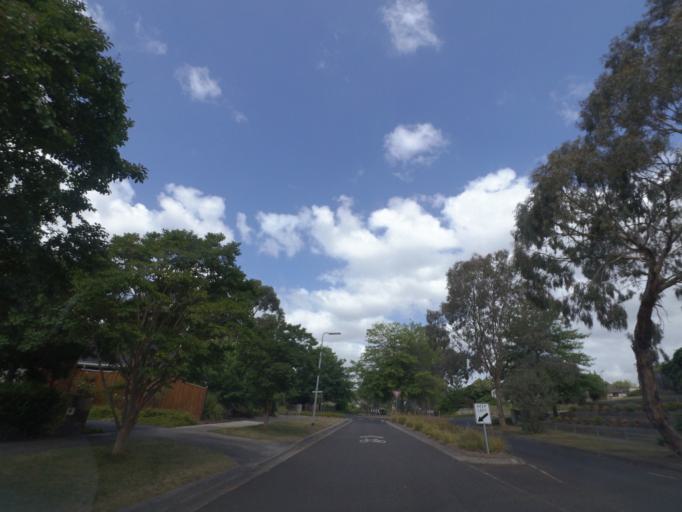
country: AU
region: Victoria
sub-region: Yarra Ranges
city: Lilydale
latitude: -37.7731
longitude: 145.3538
